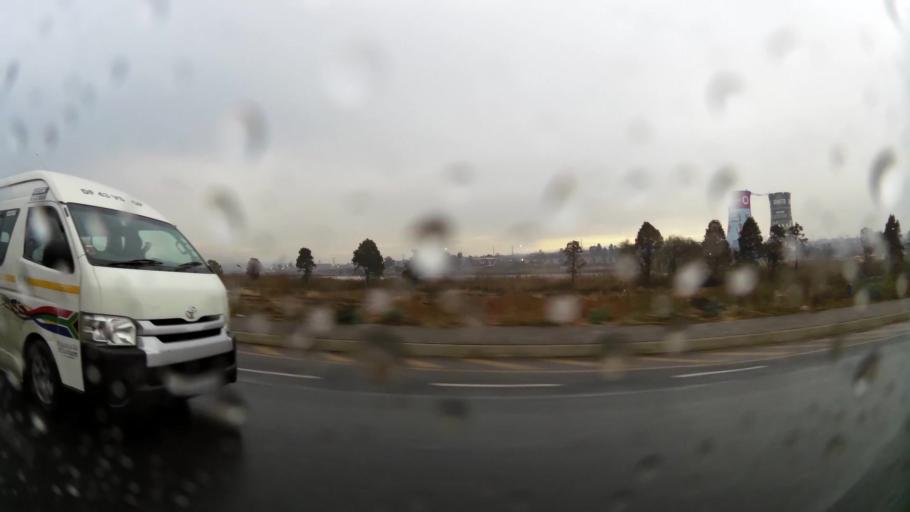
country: ZA
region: Gauteng
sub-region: City of Johannesburg Metropolitan Municipality
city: Soweto
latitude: -26.2593
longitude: 27.9225
